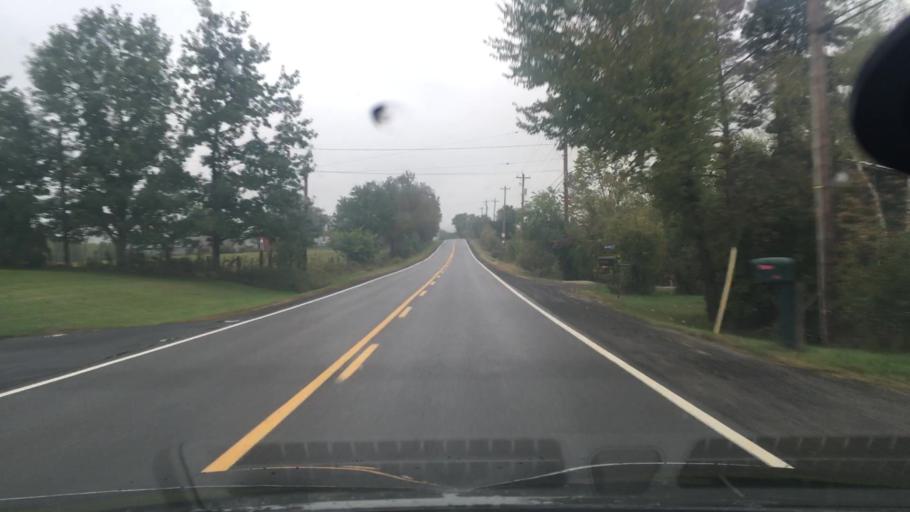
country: CA
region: Nova Scotia
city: Windsor
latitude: 44.9468
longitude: -64.1784
